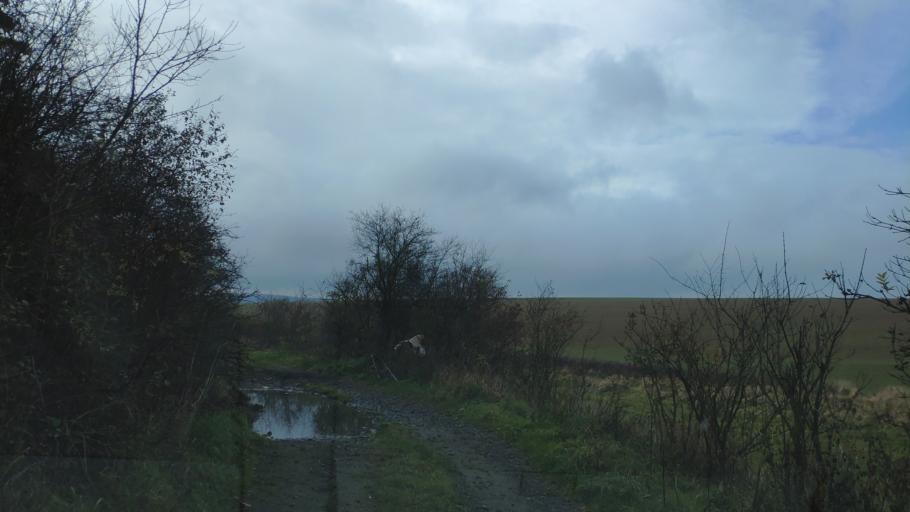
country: SK
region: Presovsky
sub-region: Okres Presov
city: Presov
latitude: 49.0242
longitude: 21.1988
